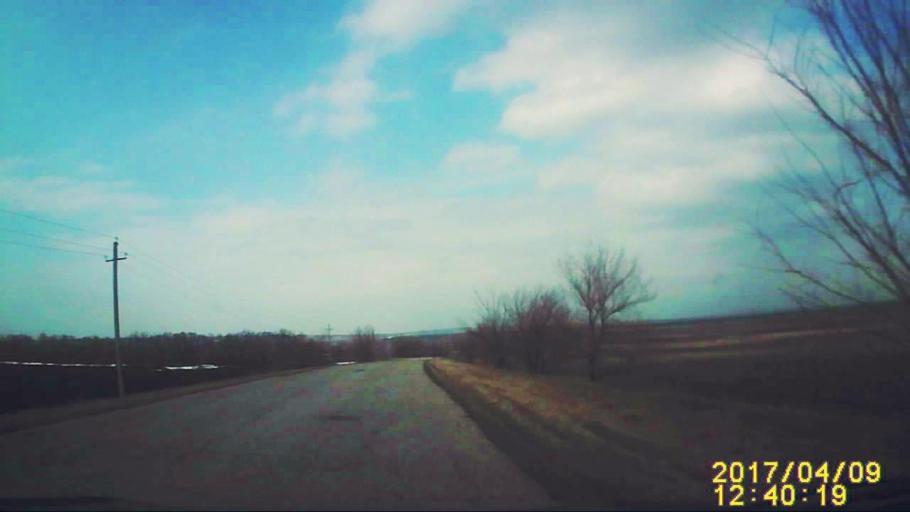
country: RU
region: Ulyanovsk
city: Ignatovka
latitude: 54.0027
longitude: 47.9470
